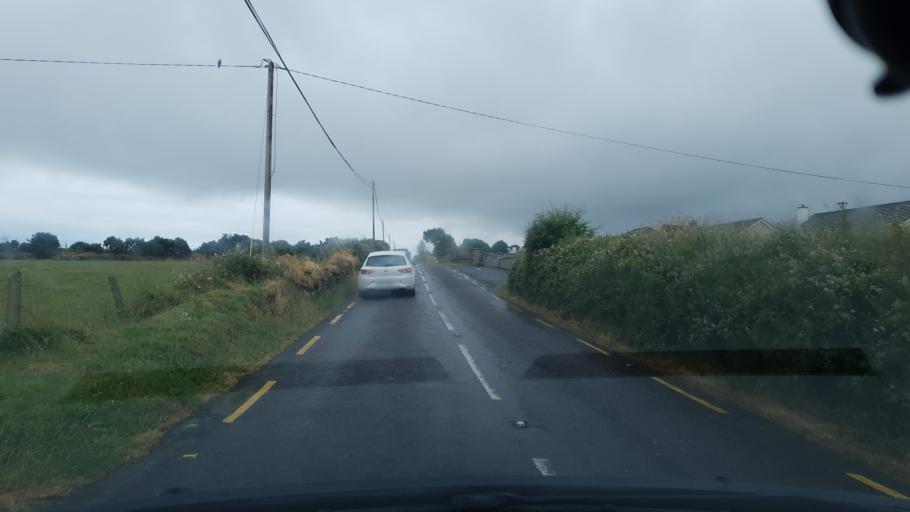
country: IE
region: Munster
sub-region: Ciarrai
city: Killorglin
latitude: 52.1640
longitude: -9.8328
